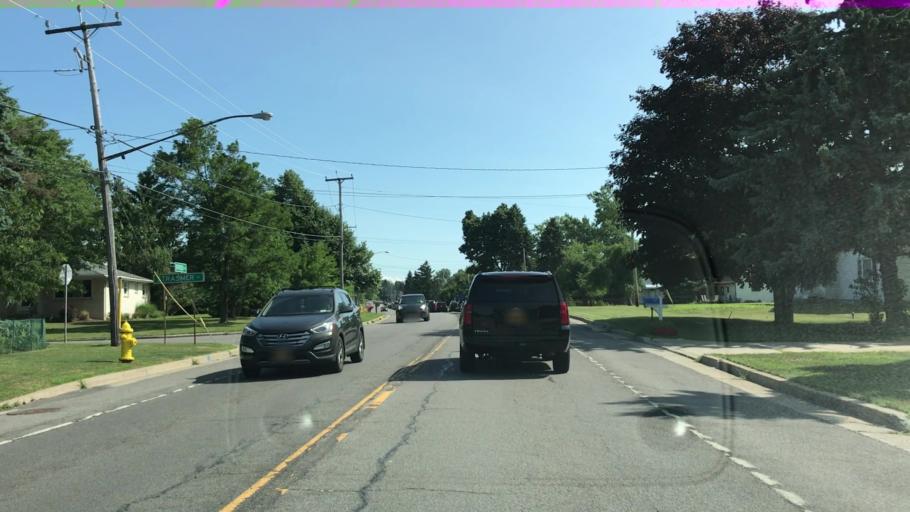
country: US
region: New York
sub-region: Erie County
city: Depew
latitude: 42.8853
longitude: -78.7089
